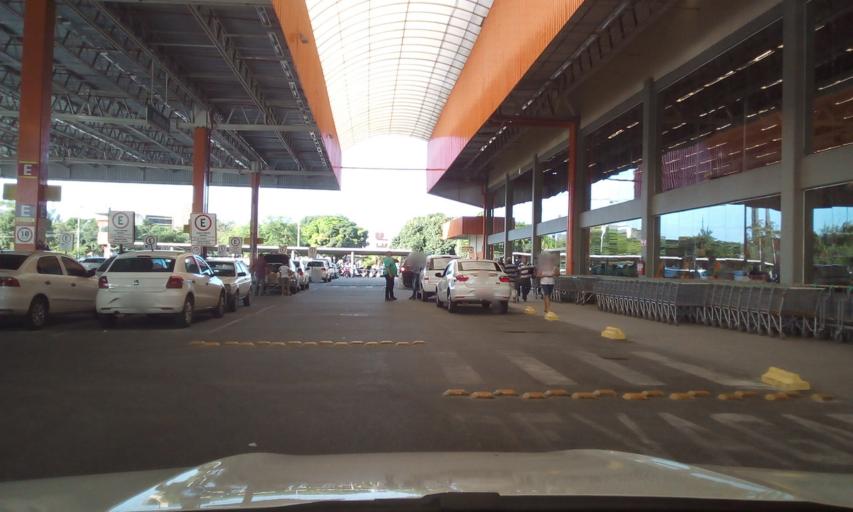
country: BR
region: Paraiba
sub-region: Joao Pessoa
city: Joao Pessoa
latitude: -7.1705
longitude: -34.8654
